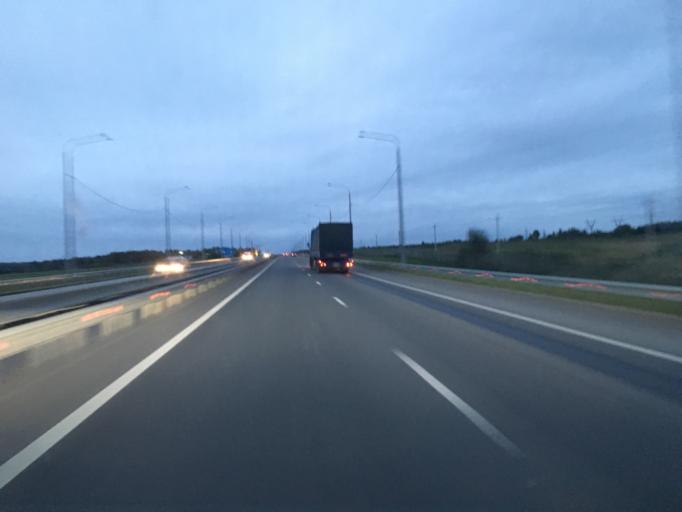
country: RU
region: Kaluga
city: Maloyaroslavets
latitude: 54.9507
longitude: 36.4466
